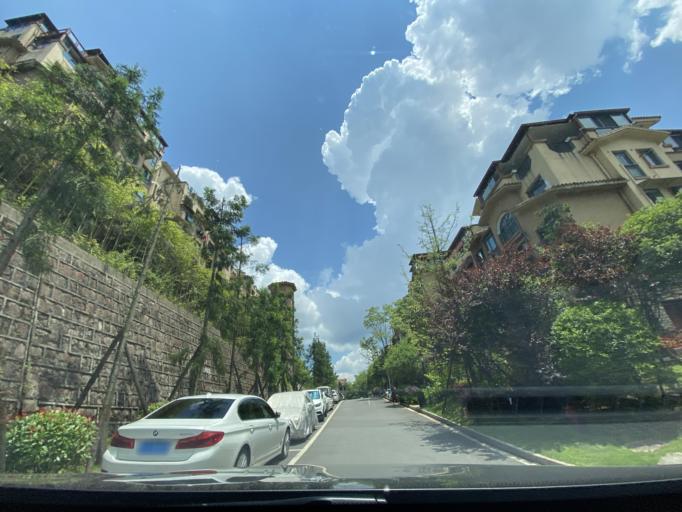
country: CN
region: Guizhou Sheng
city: Changqi
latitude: 28.5366
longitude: 105.9777
